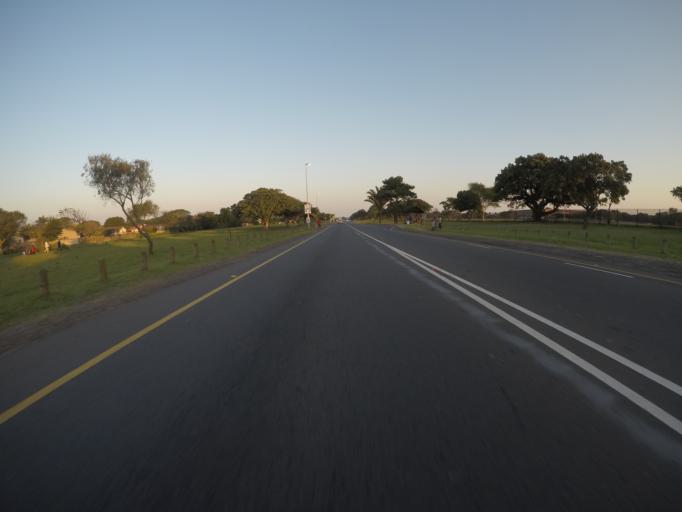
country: ZA
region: KwaZulu-Natal
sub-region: uThungulu District Municipality
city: Richards Bay
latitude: -28.7579
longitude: 32.0585
